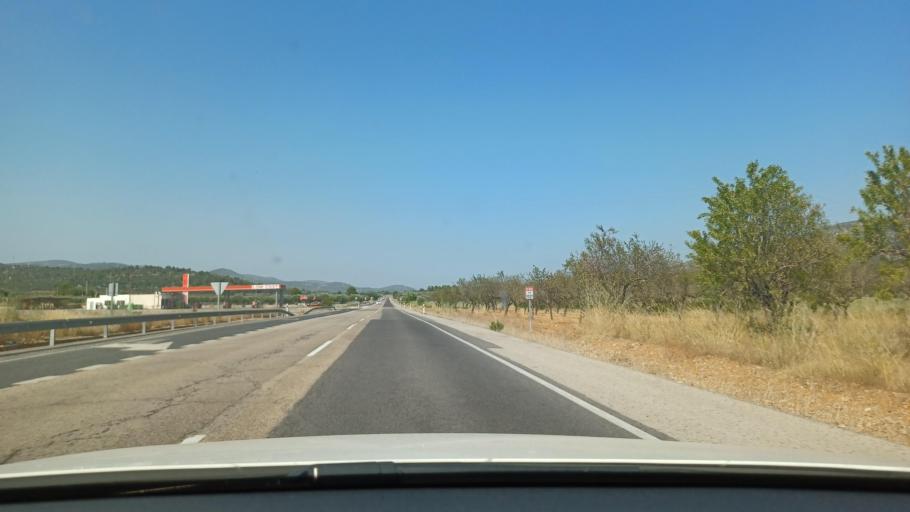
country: ES
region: Valencia
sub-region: Provincia de Castello
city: Alcala de Xivert
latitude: 40.3349
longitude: 0.2579
